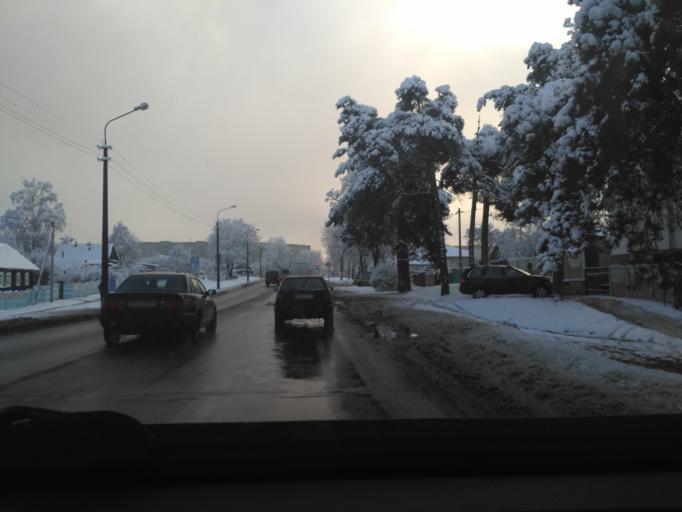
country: BY
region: Minsk
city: Horad Barysaw
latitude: 54.2276
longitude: 28.4941
